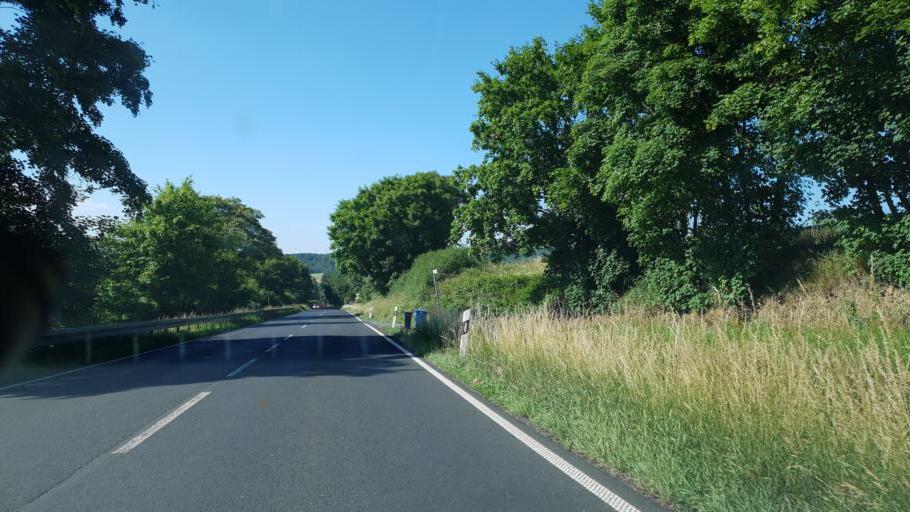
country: DE
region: Hesse
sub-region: Regierungsbezirk Darmstadt
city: Waldems
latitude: 50.2461
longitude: 8.3122
